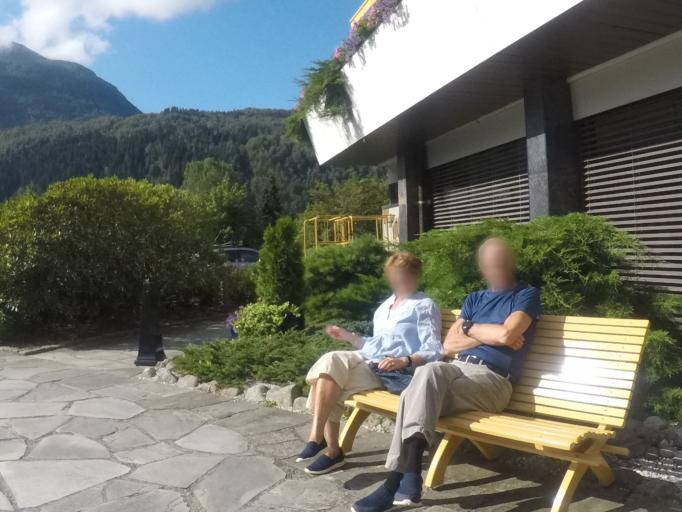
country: NO
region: Sogn og Fjordane
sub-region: Stryn
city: Stryn
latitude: 61.8728
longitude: 6.8463
